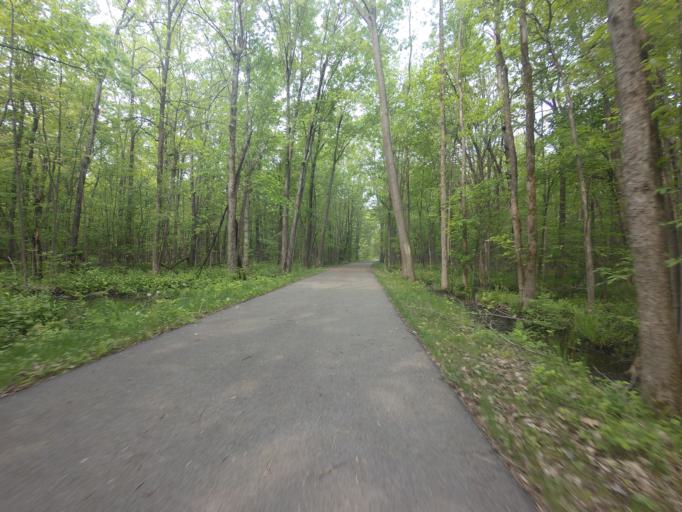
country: US
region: New York
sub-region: Jefferson County
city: Watertown
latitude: 43.9717
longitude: -75.8671
